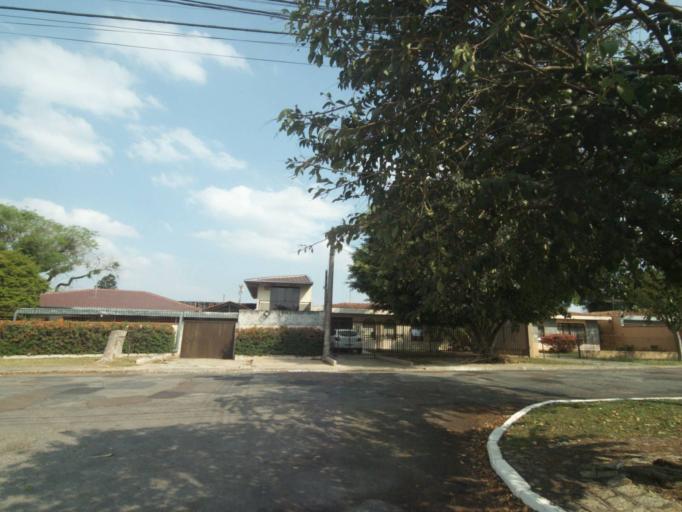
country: BR
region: Parana
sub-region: Sao Jose Dos Pinhais
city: Sao Jose dos Pinhais
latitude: -25.5132
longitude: -49.2460
